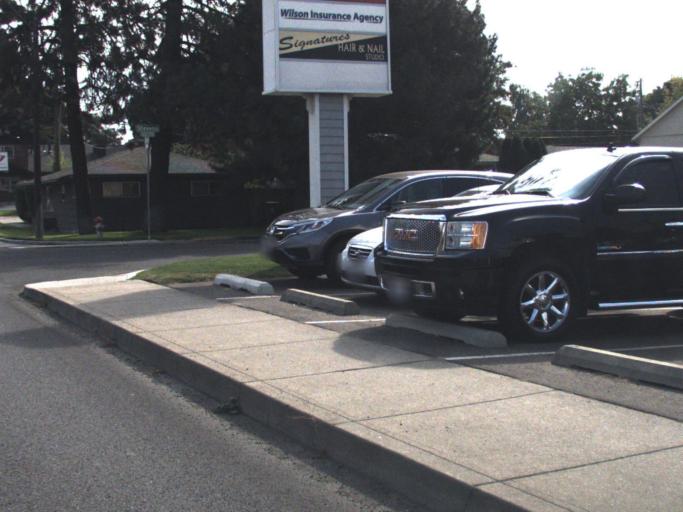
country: US
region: Washington
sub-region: Spokane County
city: Town and Country
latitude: 47.7151
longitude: -117.4194
